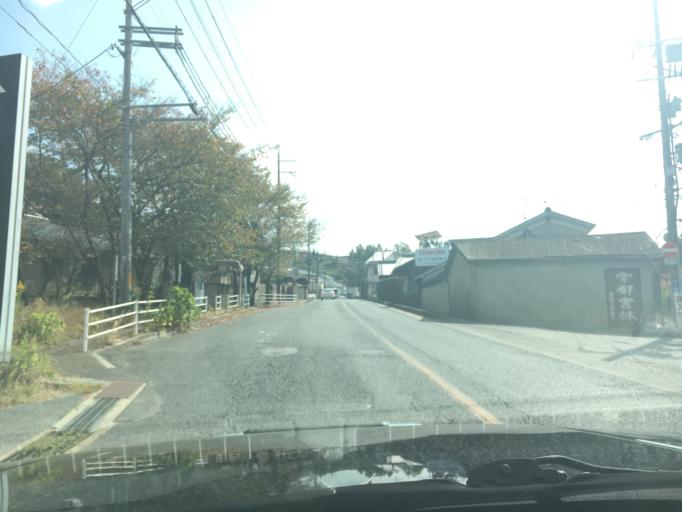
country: JP
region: Nara
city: Nara-shi
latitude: 34.7055
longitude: 135.8341
